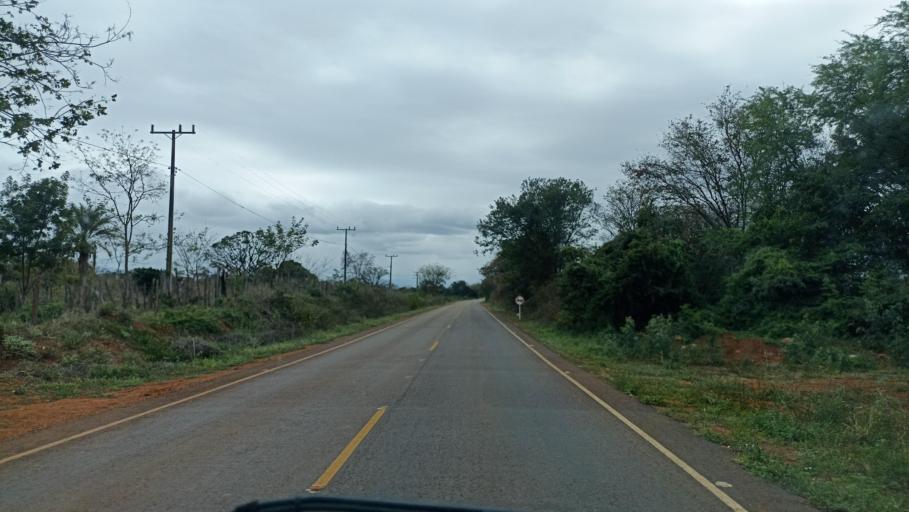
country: BR
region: Bahia
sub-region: Andarai
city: Vera Cruz
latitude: -12.9815
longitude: -41.0138
